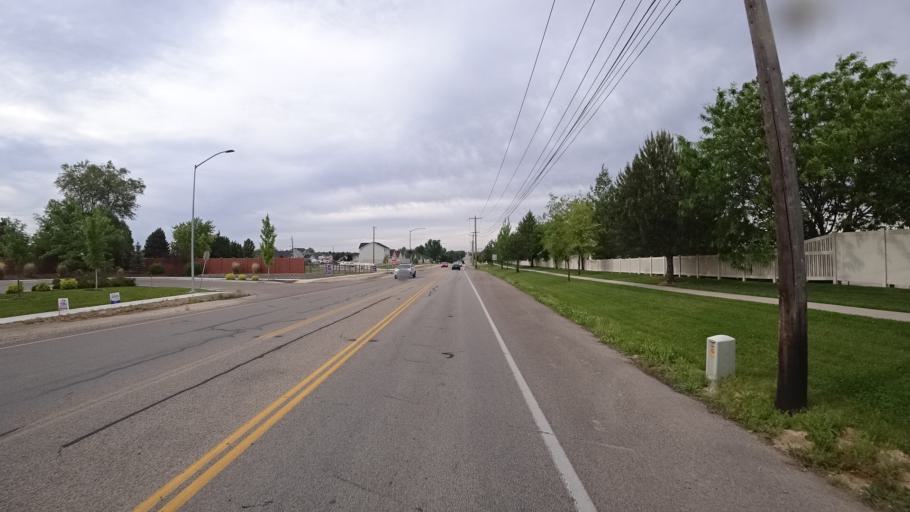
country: US
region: Idaho
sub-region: Ada County
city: Meridian
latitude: 43.5747
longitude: -116.3545
